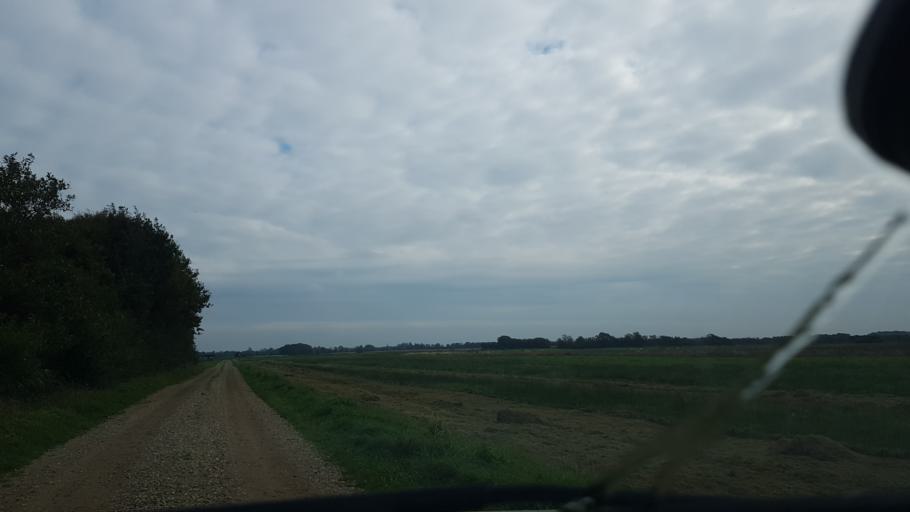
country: DK
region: South Denmark
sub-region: Esbjerg Kommune
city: Ribe
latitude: 55.3572
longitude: 8.8090
